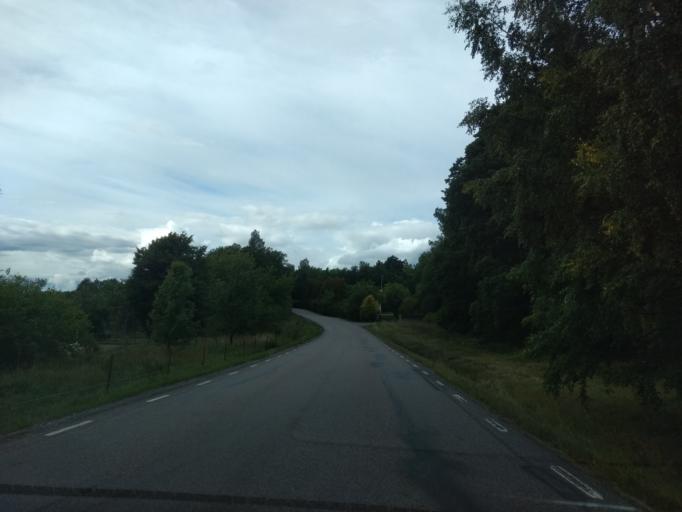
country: SE
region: Uppsala
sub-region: Habo Kommun
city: Balsta
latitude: 59.6777
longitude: 17.5361
